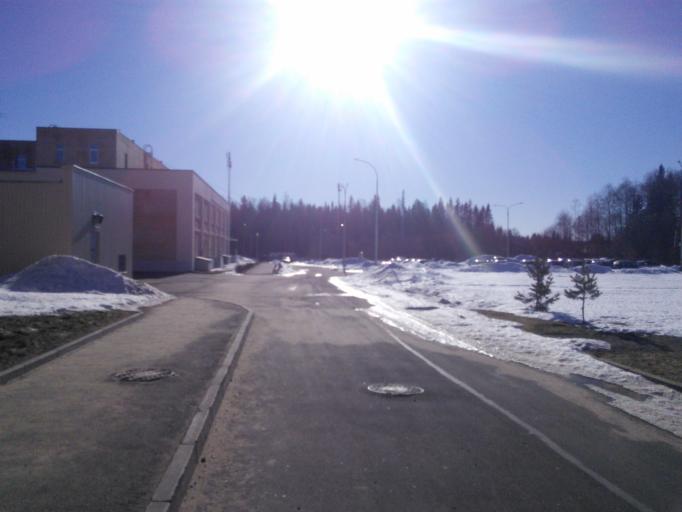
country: RU
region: Republic of Karelia
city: Petrozavodsk
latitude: 61.7725
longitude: 34.2823
